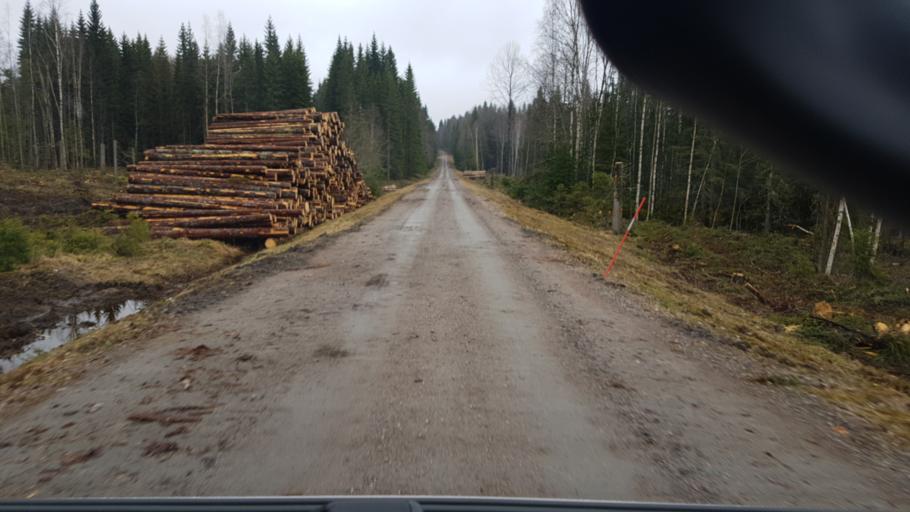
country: SE
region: Vaermland
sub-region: Eda Kommun
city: Charlottenberg
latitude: 59.9886
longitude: 12.5021
